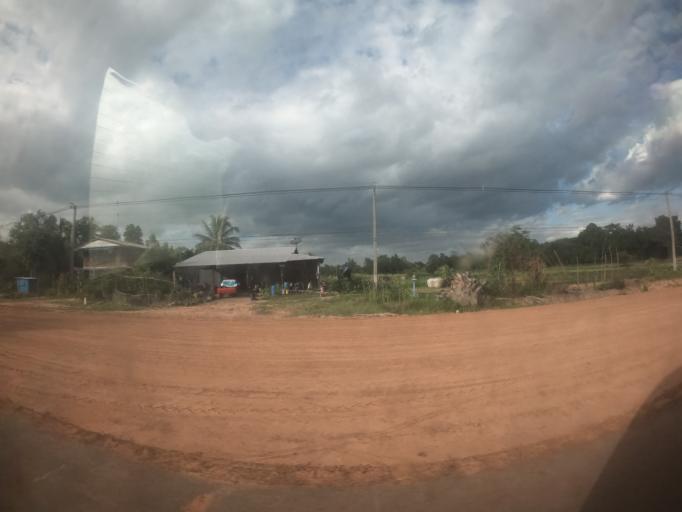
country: TH
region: Surin
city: Kap Choeng
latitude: 14.4994
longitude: 103.5647
